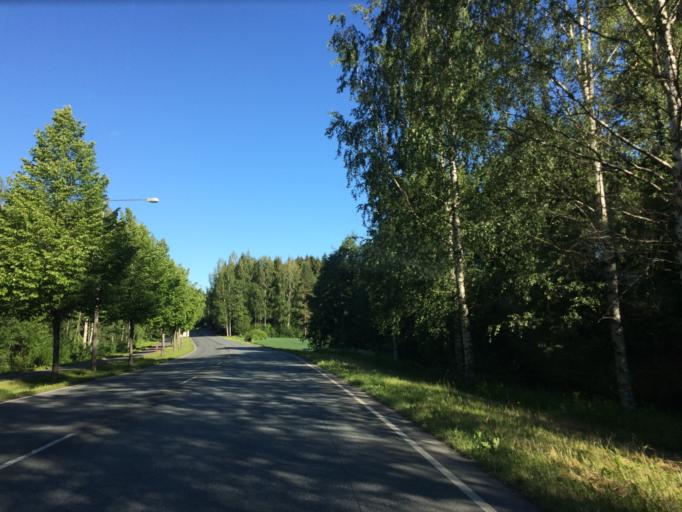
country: FI
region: Haeme
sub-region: Haemeenlinna
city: Haemeenlinna
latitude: 60.9668
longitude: 24.4451
